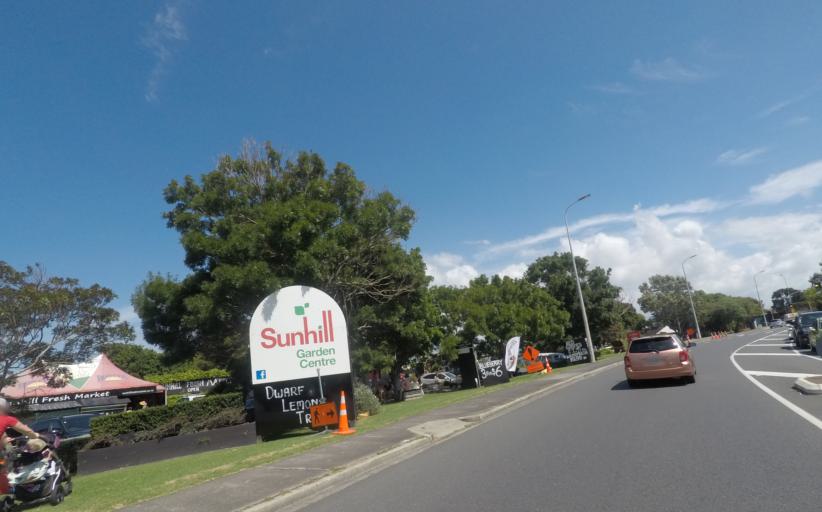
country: NZ
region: Auckland
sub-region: Auckland
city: Tamaki
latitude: -36.8700
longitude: 174.8457
